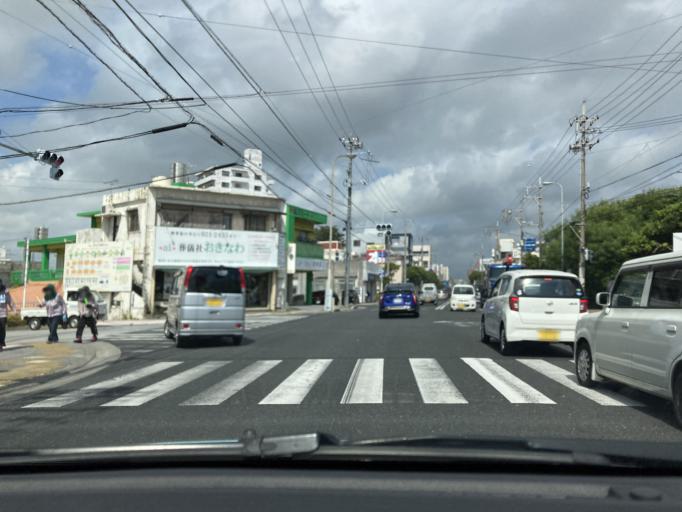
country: JP
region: Okinawa
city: Okinawa
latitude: 26.3349
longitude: 127.8179
